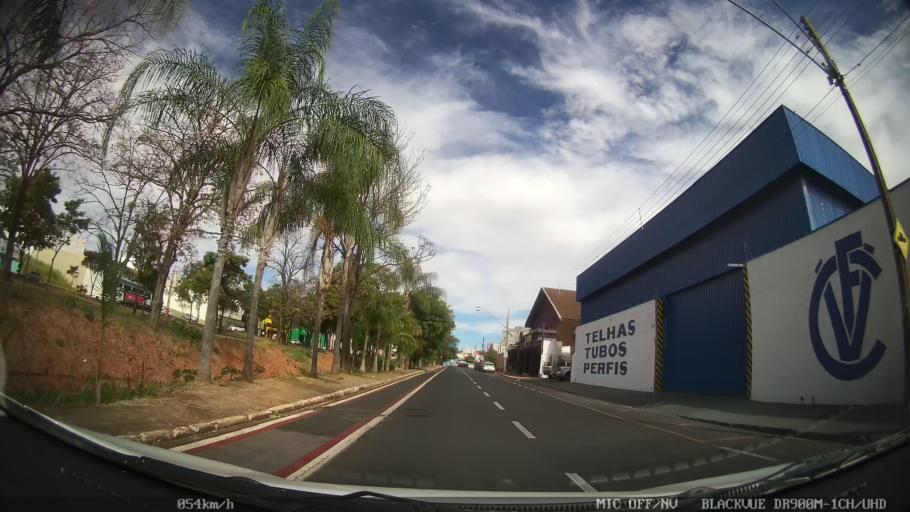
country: BR
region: Sao Paulo
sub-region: Catanduva
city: Catanduva
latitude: -21.1457
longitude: -48.9739
